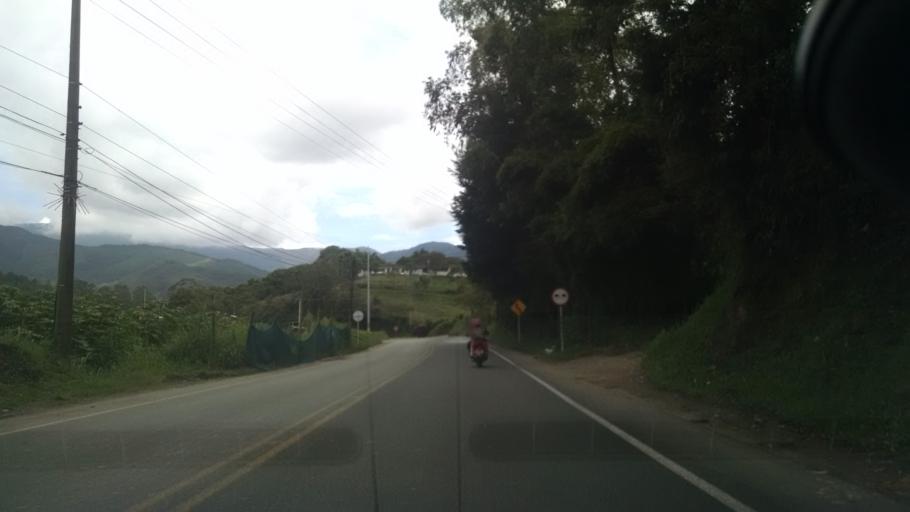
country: CO
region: Antioquia
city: Caldas
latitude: 6.0608
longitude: -75.6319
